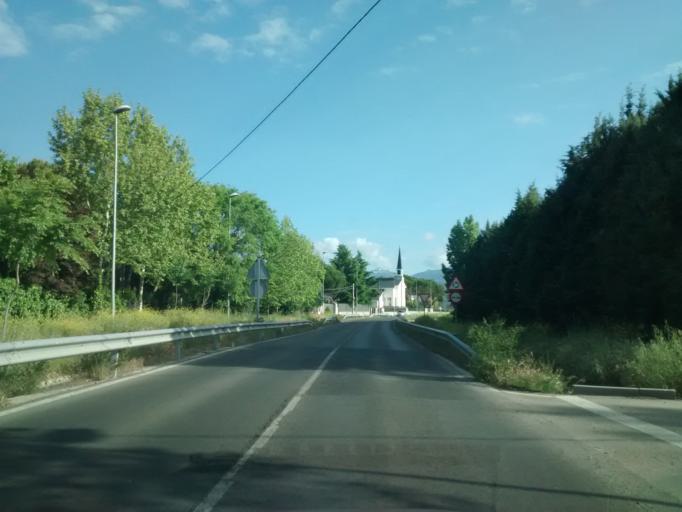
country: ES
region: Madrid
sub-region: Provincia de Madrid
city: Alpedrete
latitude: 40.6426
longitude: -4.0217
